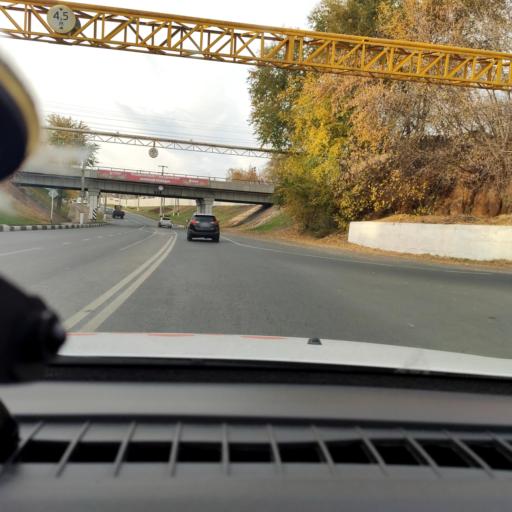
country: RU
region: Samara
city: Novokuybyshevsk
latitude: 53.1192
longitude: 49.9382
